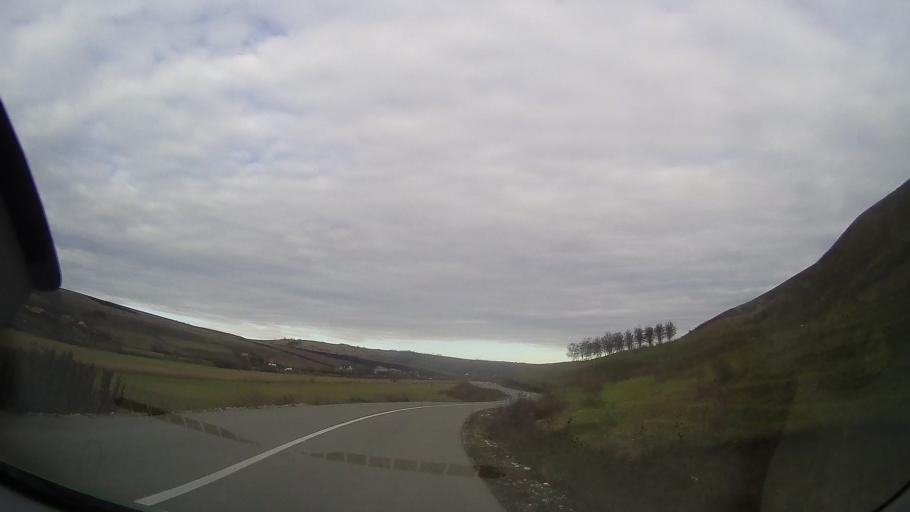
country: RO
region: Bistrita-Nasaud
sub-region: Comuna Silvasu de Campie
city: Silvasu de Campie
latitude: 46.7874
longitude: 24.2859
